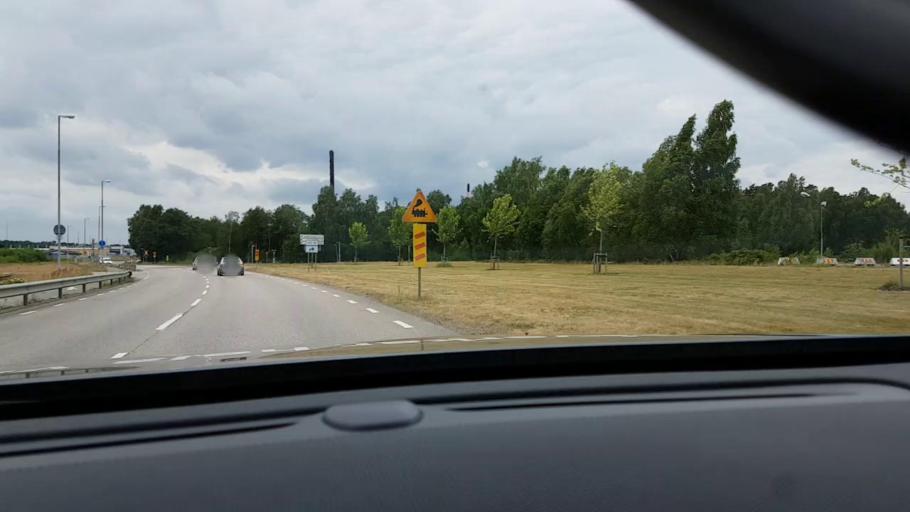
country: SE
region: Skane
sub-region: Hassleholms Kommun
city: Hassleholm
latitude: 56.1592
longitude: 13.8040
